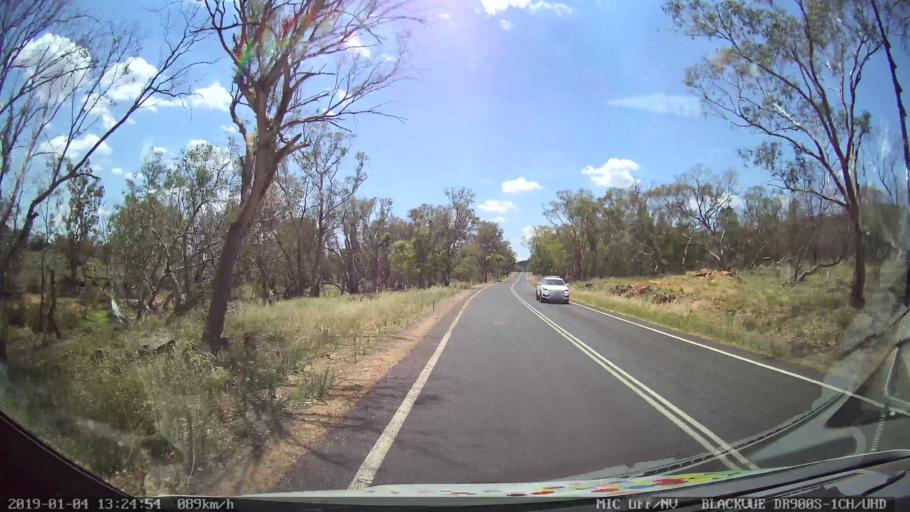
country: AU
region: New South Wales
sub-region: Parkes
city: Peak Hill
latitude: -32.6995
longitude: 148.5538
